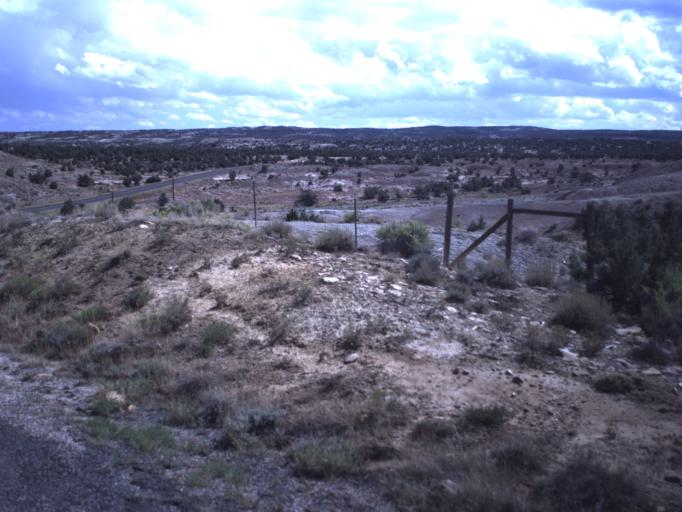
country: US
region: Utah
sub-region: Duchesne County
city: Duchesne
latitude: 40.1850
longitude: -110.4493
